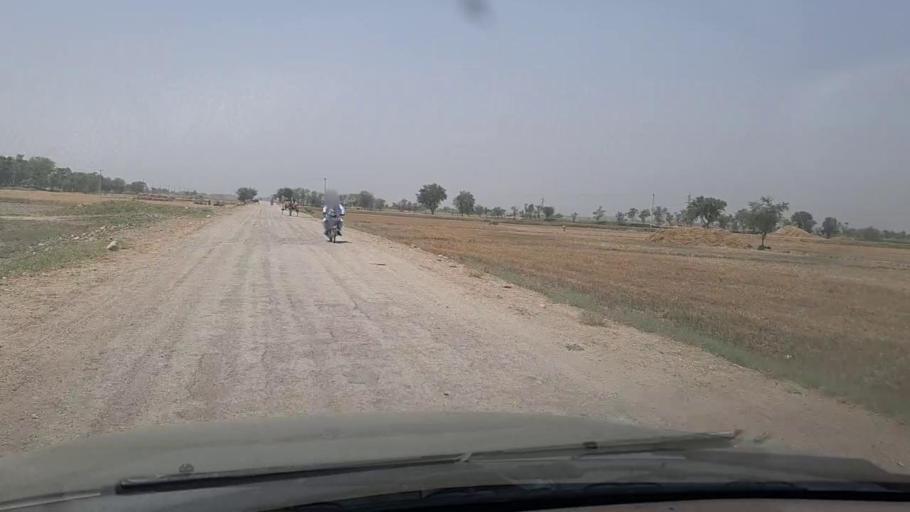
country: PK
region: Sindh
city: Ratodero
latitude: 27.7943
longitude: 68.2420
